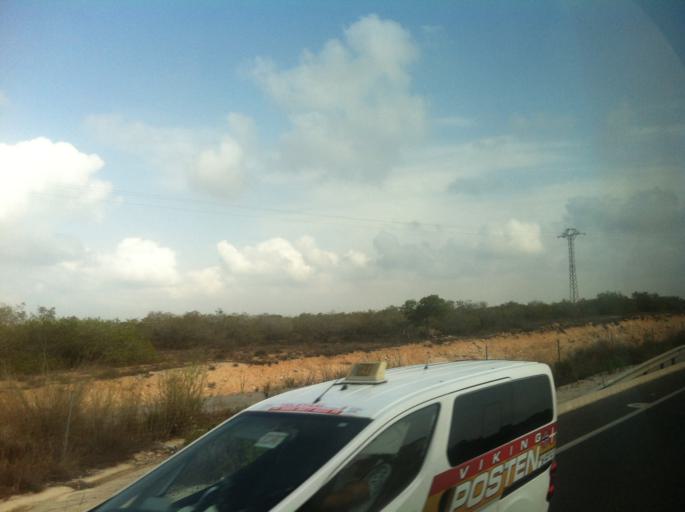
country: ES
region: Valencia
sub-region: Provincia de Alicante
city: Guardamar del Segura
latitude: 38.1350
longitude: -0.6583
